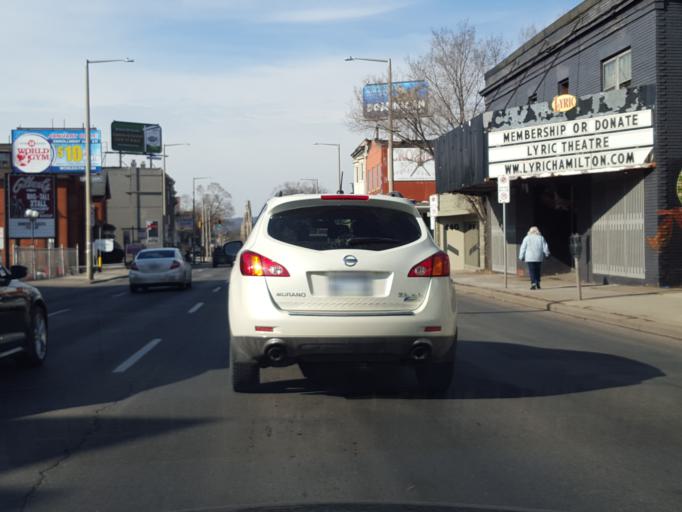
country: CA
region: Ontario
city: Hamilton
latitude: 43.2603
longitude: -79.8820
